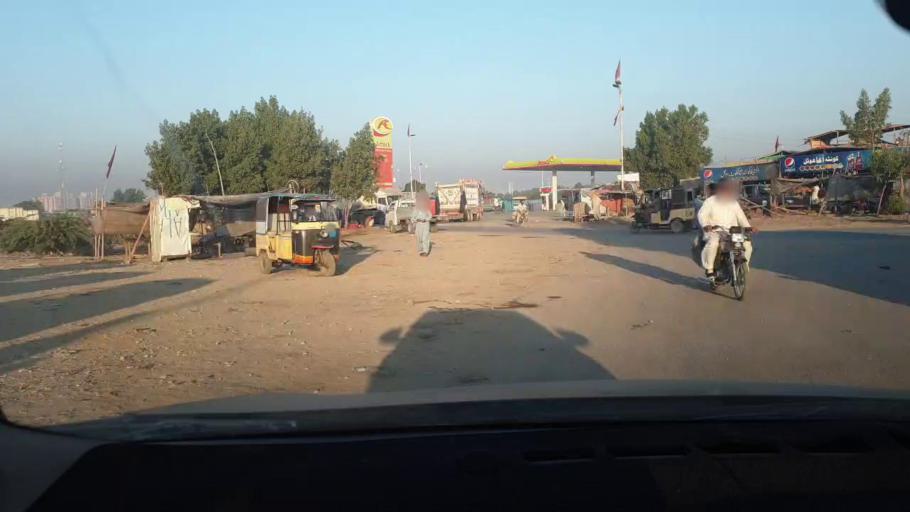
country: PK
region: Sindh
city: Malir Cantonment
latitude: 24.9952
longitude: 67.1423
